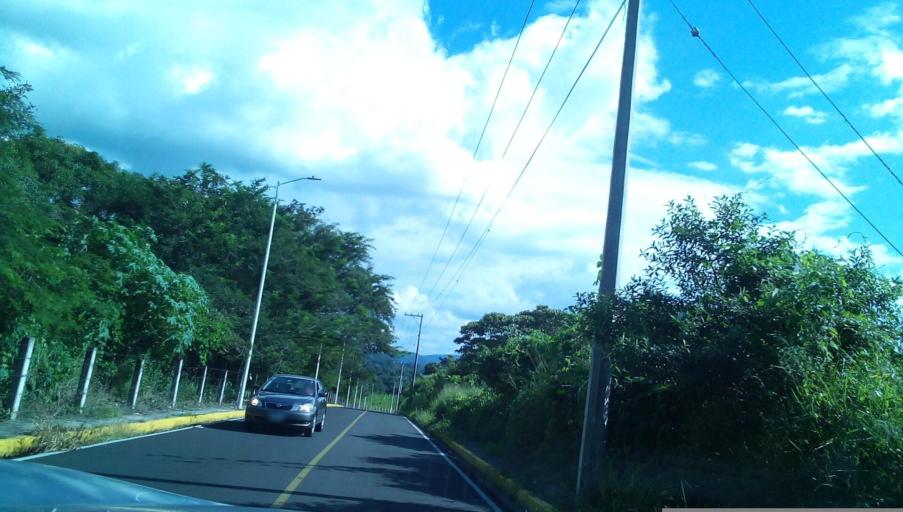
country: MX
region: Veracruz
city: Cordoba
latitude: 18.8993
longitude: -96.9228
